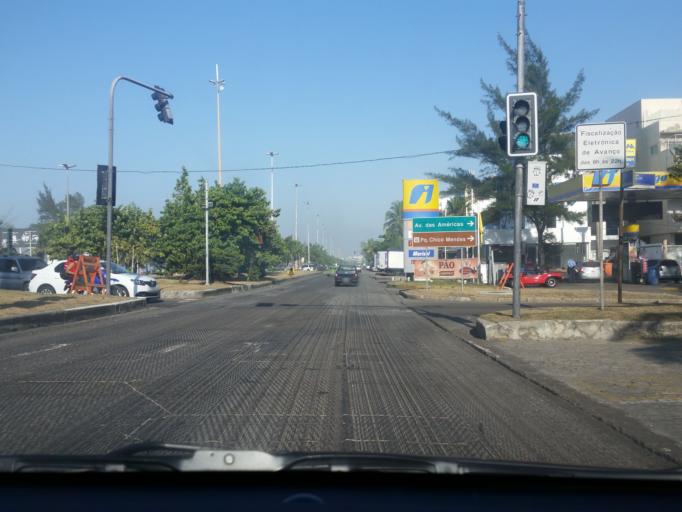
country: BR
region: Rio de Janeiro
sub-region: Nilopolis
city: Nilopolis
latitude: -23.0247
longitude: -43.4569
